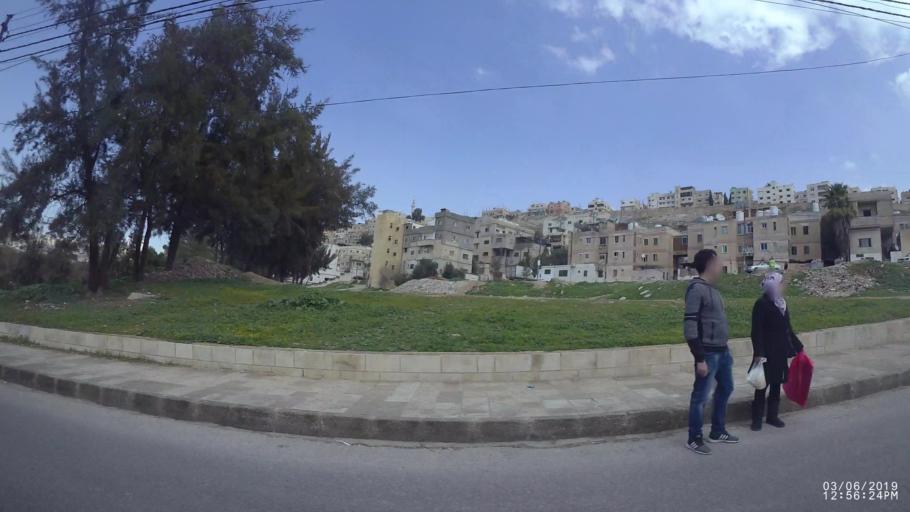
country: JO
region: Amman
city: Amman
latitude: 31.9806
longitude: 35.9774
